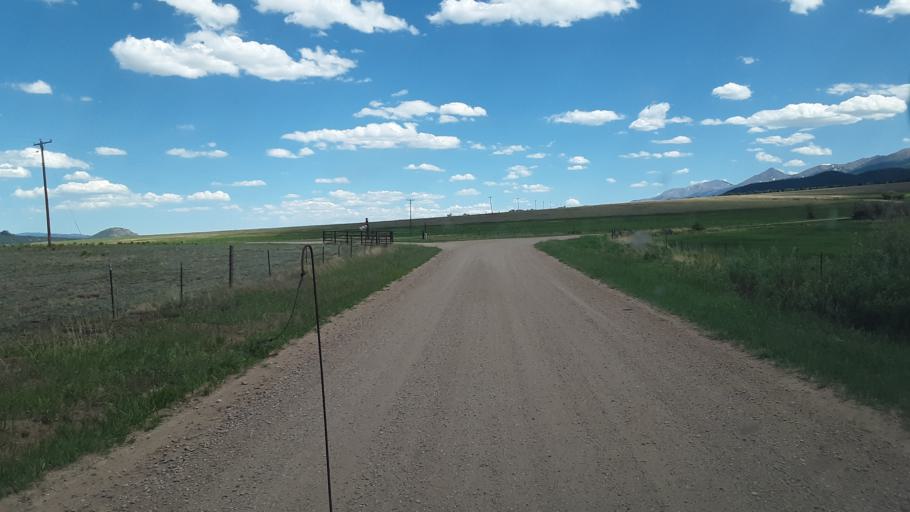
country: US
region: Colorado
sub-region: Custer County
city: Westcliffe
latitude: 38.2554
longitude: -105.6100
